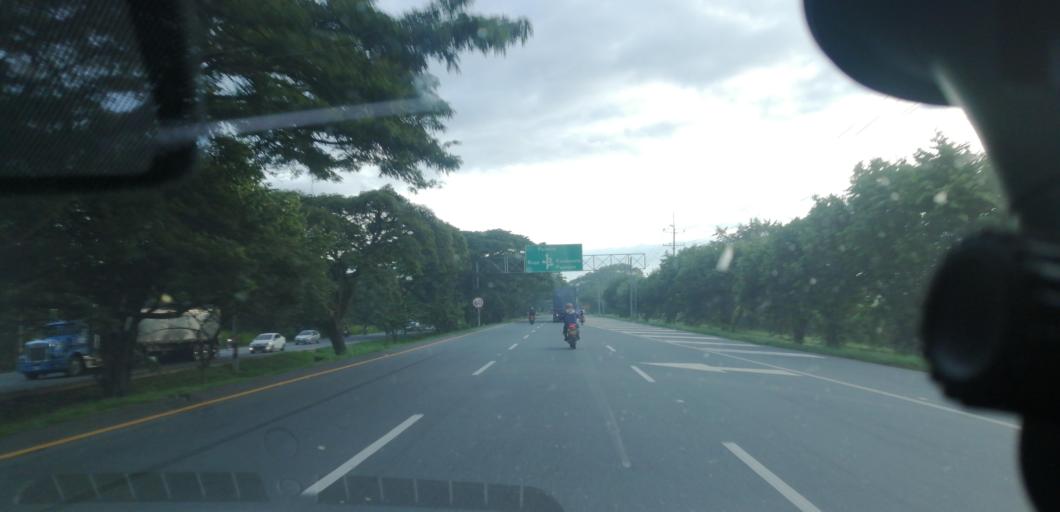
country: CO
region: Valle del Cauca
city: Palmira
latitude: 3.5234
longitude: -76.3417
